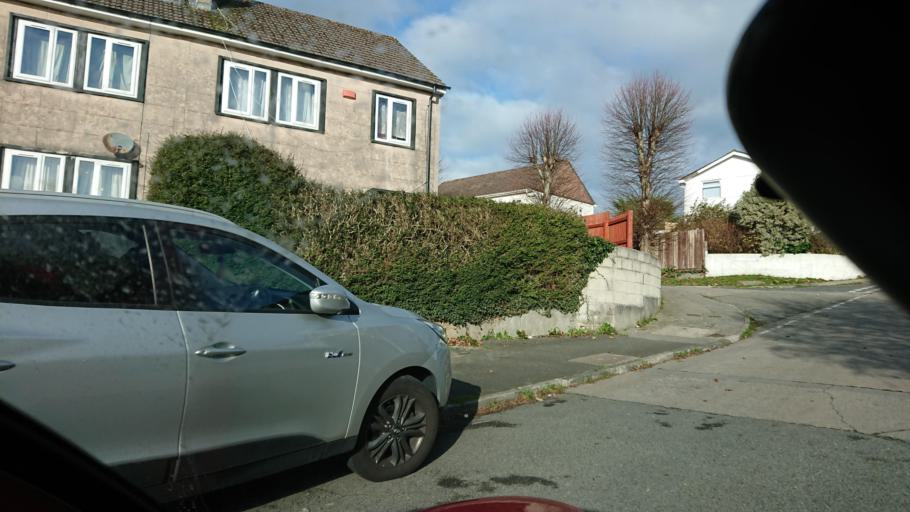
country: GB
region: England
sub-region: Cornwall
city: Torpoint
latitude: 50.4112
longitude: -4.1698
